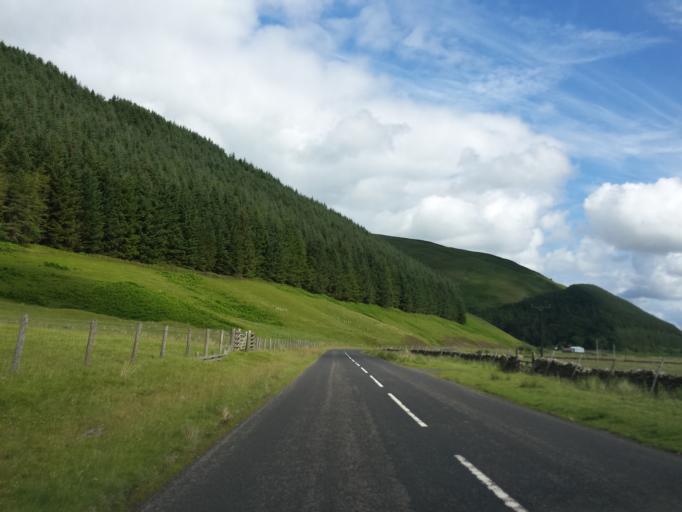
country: GB
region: Scotland
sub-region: The Scottish Borders
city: Peebles
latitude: 55.4517
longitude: -3.2214
